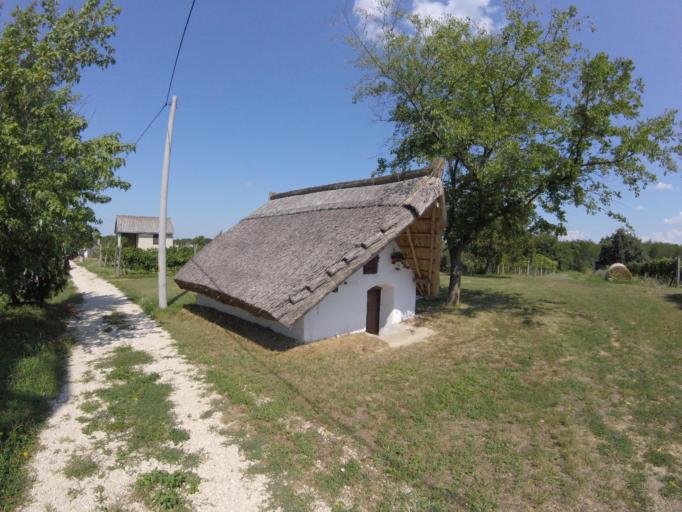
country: HU
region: Gyor-Moson-Sopron
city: Tet
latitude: 47.4738
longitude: 17.4590
